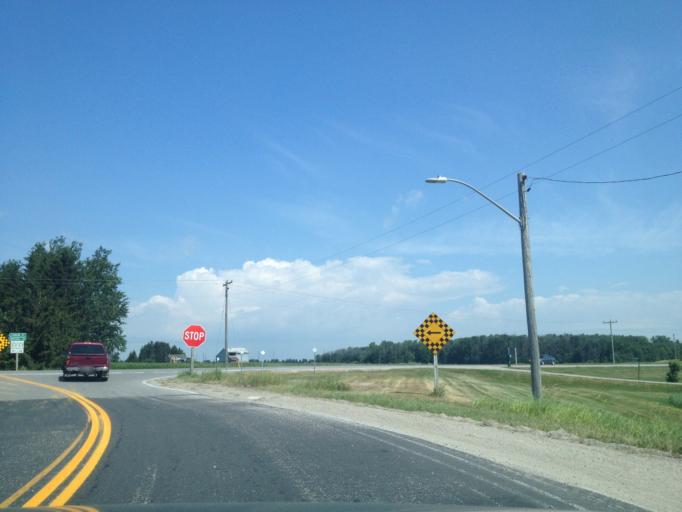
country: CA
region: Ontario
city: Huron East
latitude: 43.4347
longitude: -81.2255
